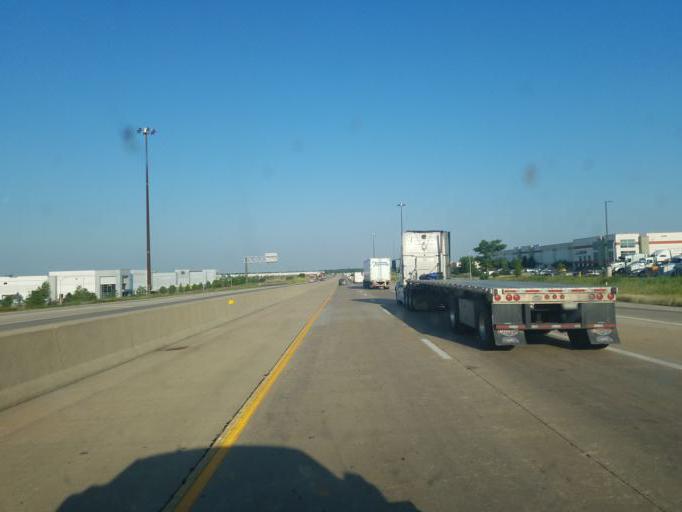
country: US
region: Illinois
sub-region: Grundy County
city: Minooka
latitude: 41.4623
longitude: -88.2754
